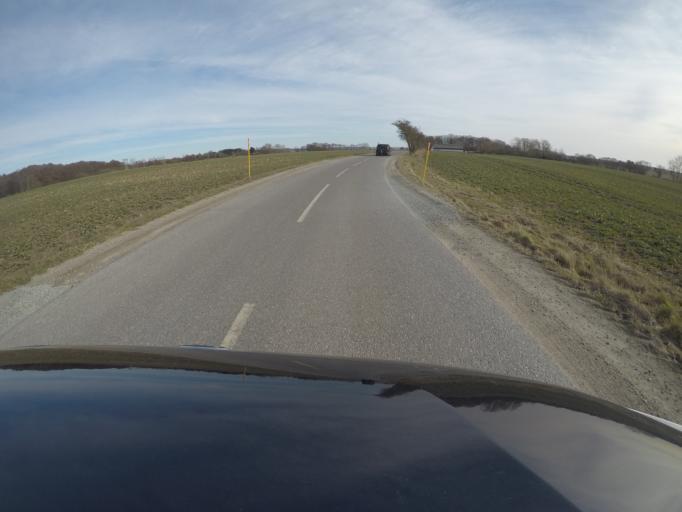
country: DK
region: Capital Region
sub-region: Halsnaes Kommune
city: Liseleje
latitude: 55.9726
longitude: 11.9688
